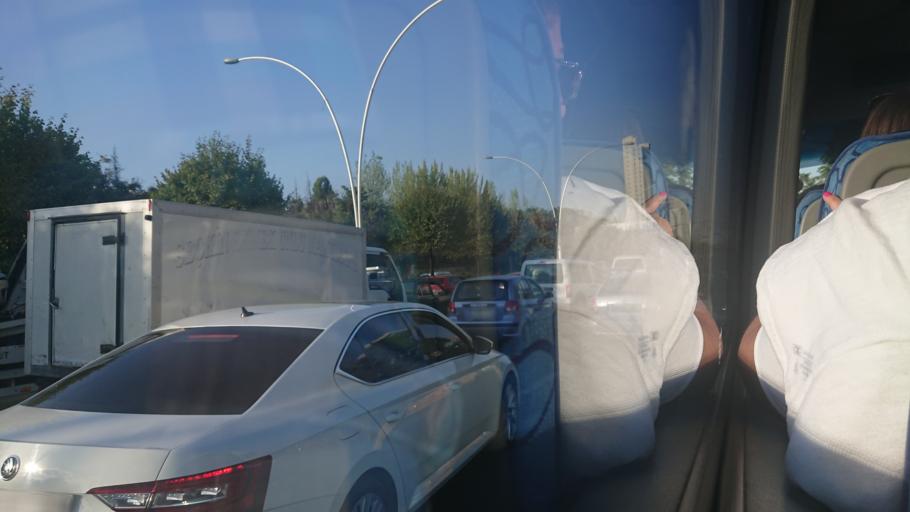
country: TR
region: Ankara
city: Ankara
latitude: 39.9336
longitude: 32.8214
